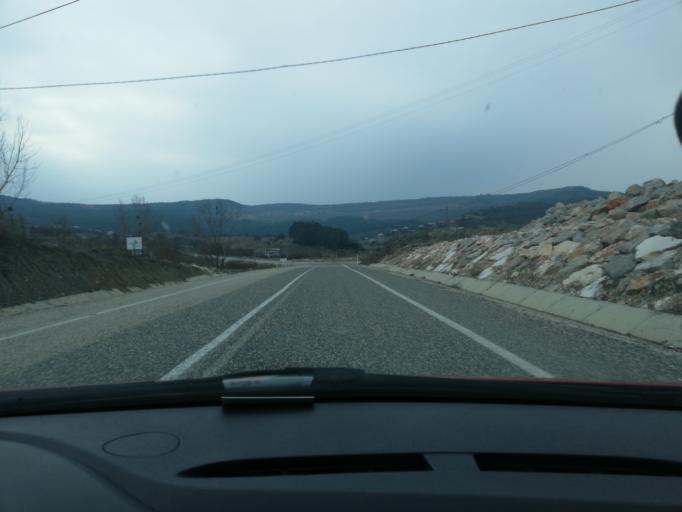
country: TR
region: Kastamonu
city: Pinarbasi
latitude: 41.5897
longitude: 33.0930
